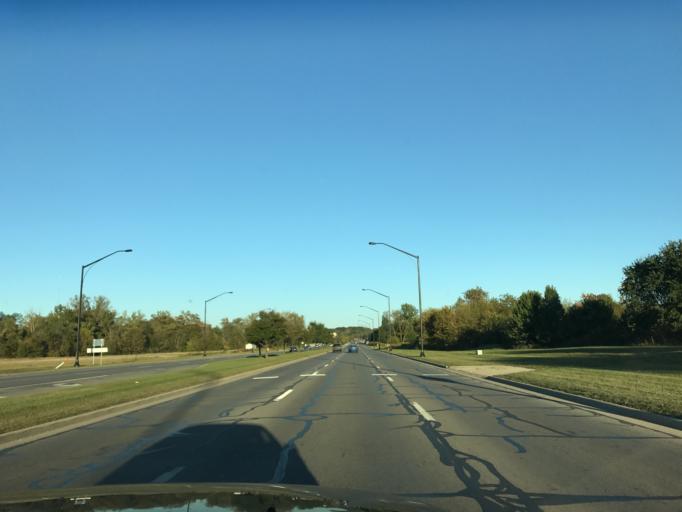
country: US
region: Ohio
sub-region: Franklin County
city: Westerville
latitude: 40.1457
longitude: -82.9551
